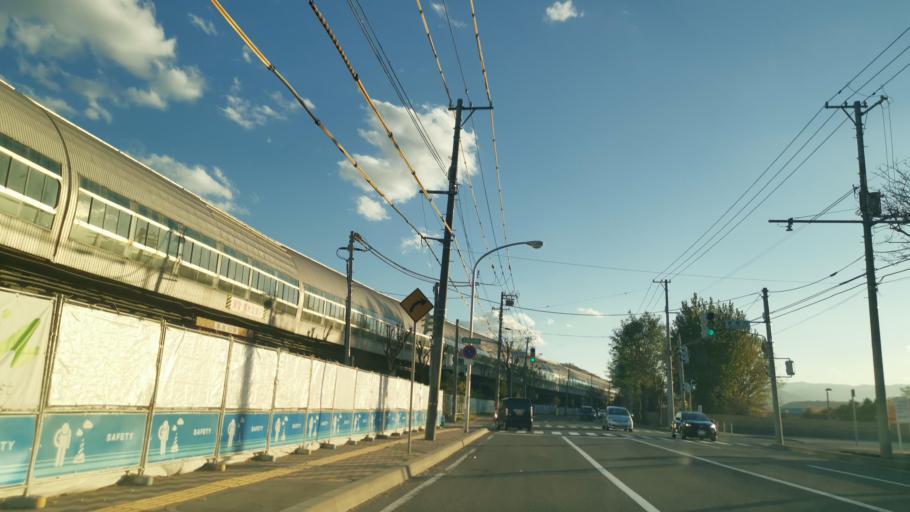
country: JP
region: Hokkaido
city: Sapporo
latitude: 43.0047
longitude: 141.3641
